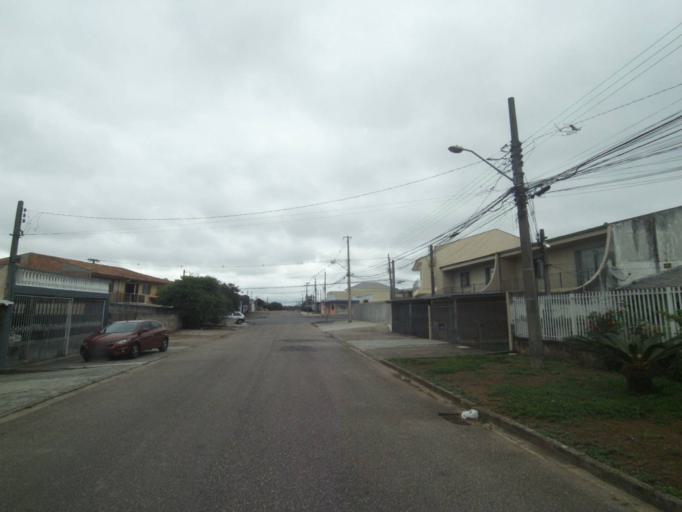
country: BR
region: Parana
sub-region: Sao Jose Dos Pinhais
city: Sao Jose dos Pinhais
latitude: -25.5381
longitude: -49.2800
